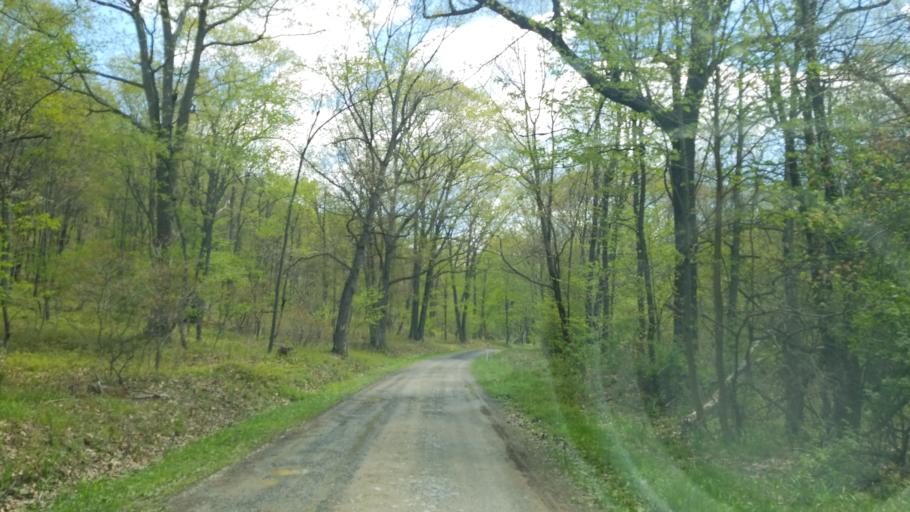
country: US
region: Pennsylvania
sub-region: Clearfield County
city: Shiloh
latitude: 41.2098
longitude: -78.1464
